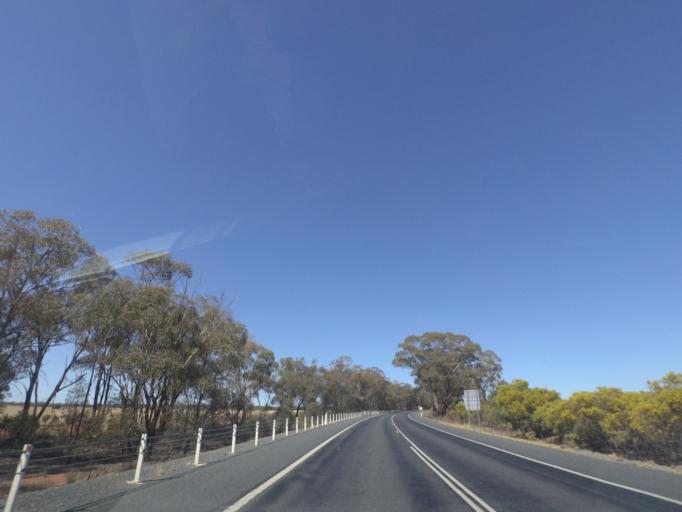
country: AU
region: New South Wales
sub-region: Bland
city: West Wyalong
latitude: -34.1137
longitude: 147.1376
